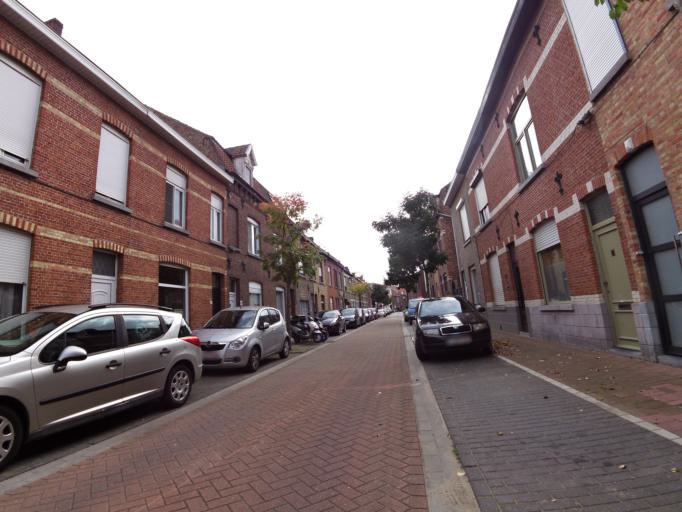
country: BE
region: Flanders
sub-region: Provincie West-Vlaanderen
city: Brugge
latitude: 51.1967
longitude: 3.2348
